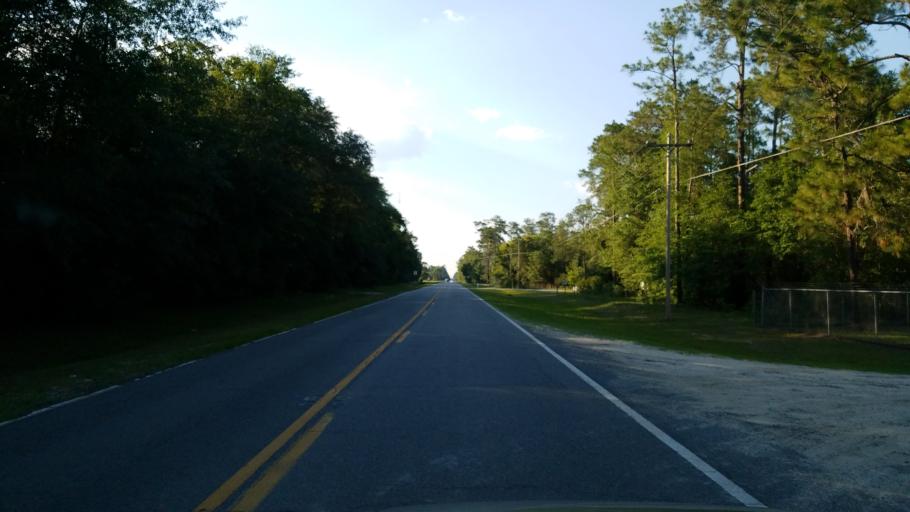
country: US
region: Georgia
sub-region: Lanier County
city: Lakeland
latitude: 31.0531
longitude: -83.0695
